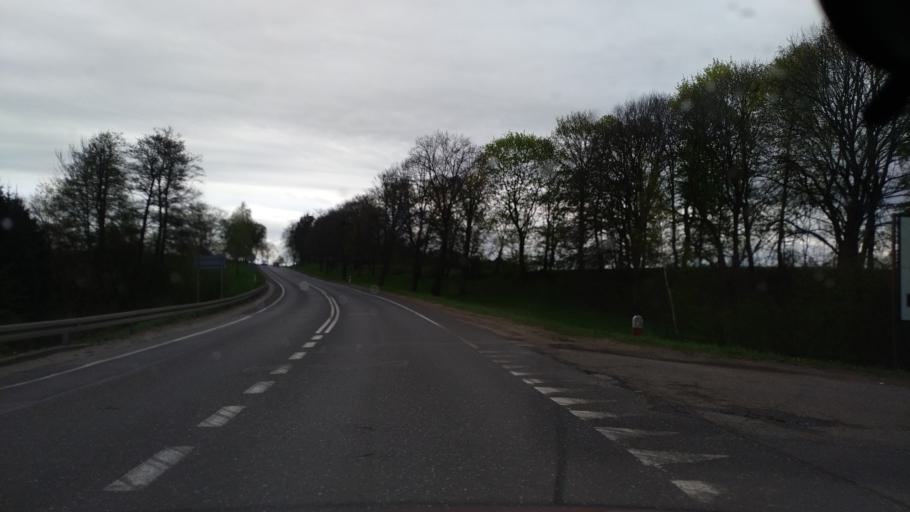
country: PL
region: Pomeranian Voivodeship
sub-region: Powiat starogardzki
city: Starogard Gdanski
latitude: 53.9464
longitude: 18.4676
